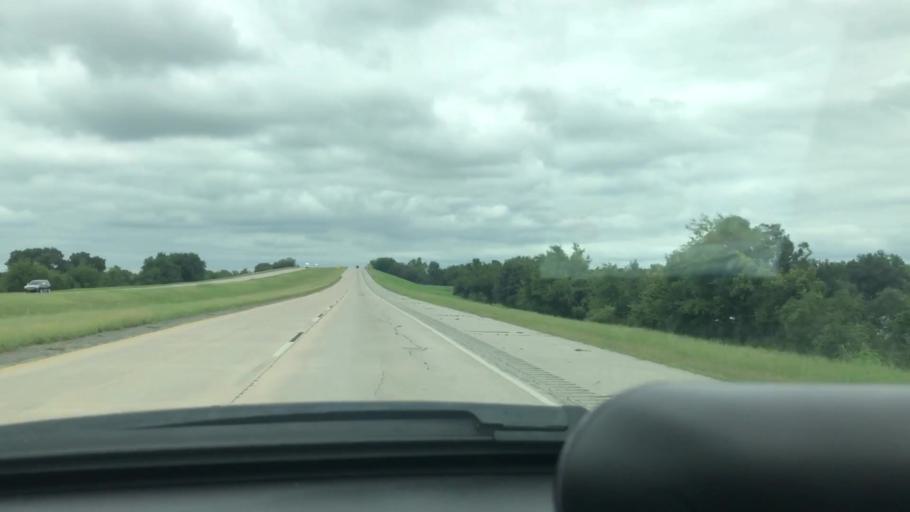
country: US
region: Oklahoma
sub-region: Wagoner County
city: Wagoner
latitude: 35.8784
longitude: -95.4030
